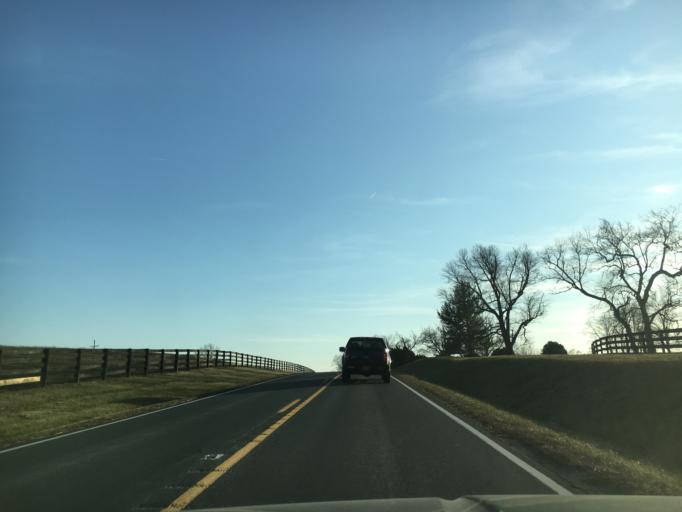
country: US
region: Virginia
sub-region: Rappahannock County
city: Washington
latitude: 38.8046
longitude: -78.1058
